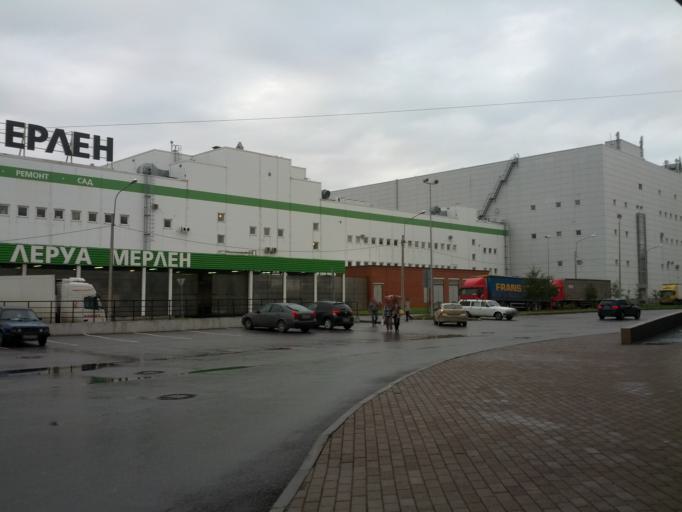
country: RU
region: St.-Petersburg
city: Obukhovo
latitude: 59.9099
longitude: 30.4467
